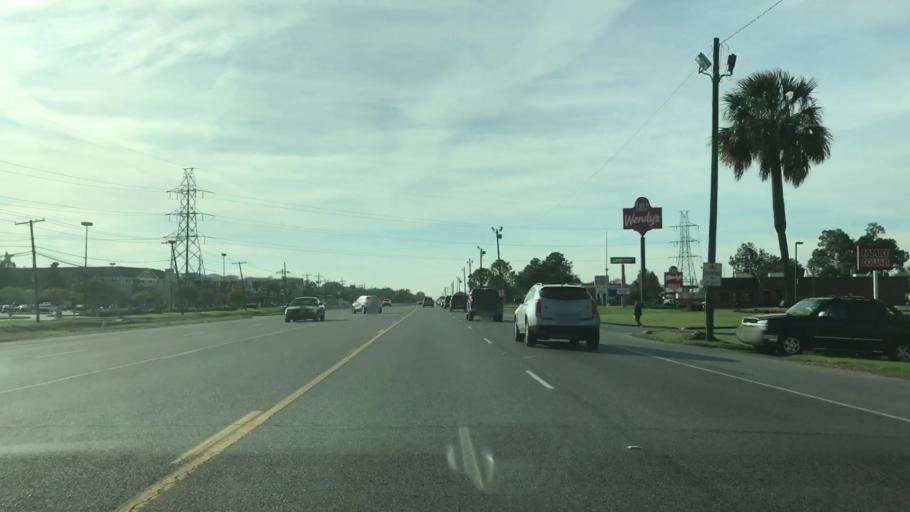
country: US
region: Louisiana
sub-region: Jefferson Parish
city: Avondale
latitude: 29.9100
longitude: -90.2038
